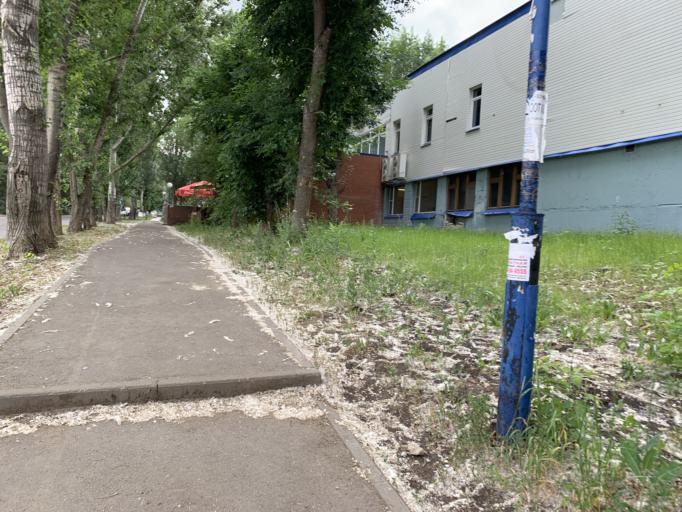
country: RU
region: Samara
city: Samara
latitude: 53.2134
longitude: 50.1732
